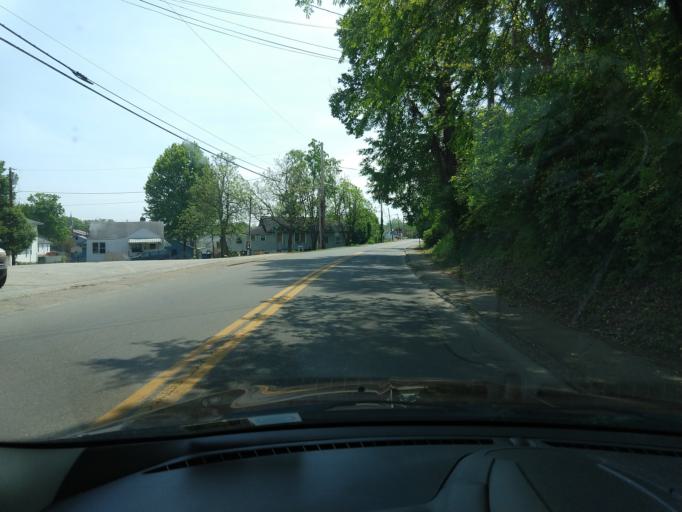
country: US
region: West Virginia
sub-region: Kanawha County
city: Saint Albans
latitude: 38.3800
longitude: -81.8211
